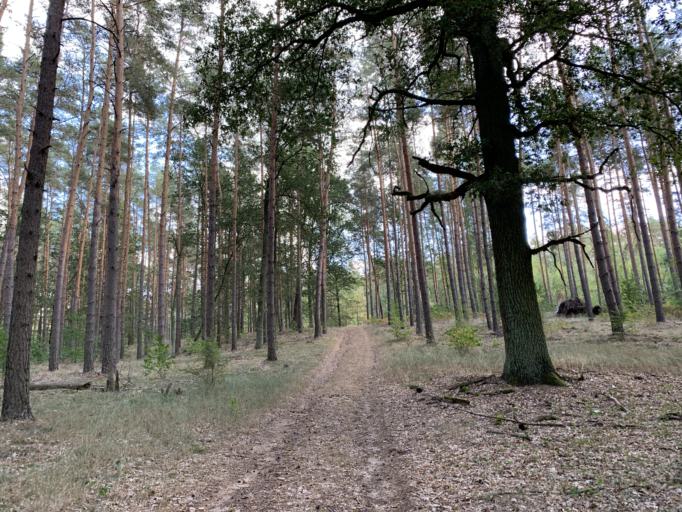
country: DE
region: Brandenburg
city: Michendorf
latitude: 52.3064
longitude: 12.9759
